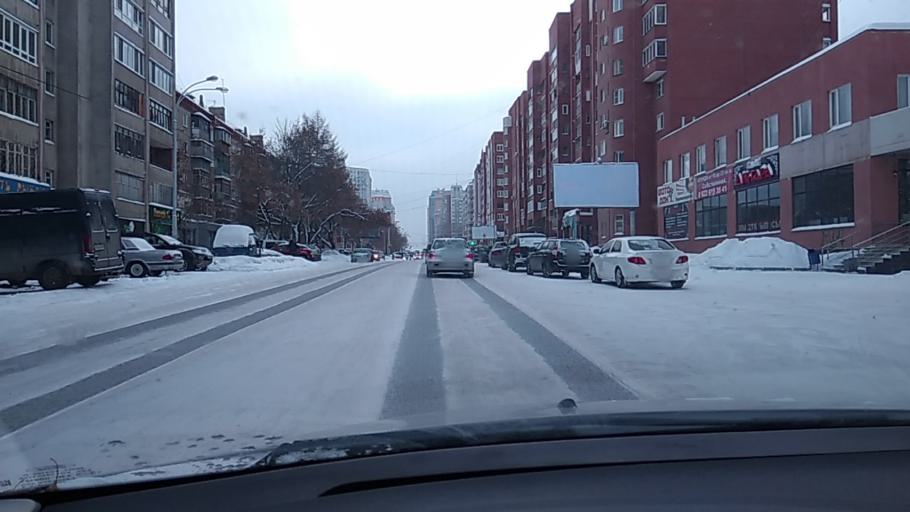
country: RU
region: Sverdlovsk
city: Yekaterinburg
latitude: 56.8114
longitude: 60.6002
